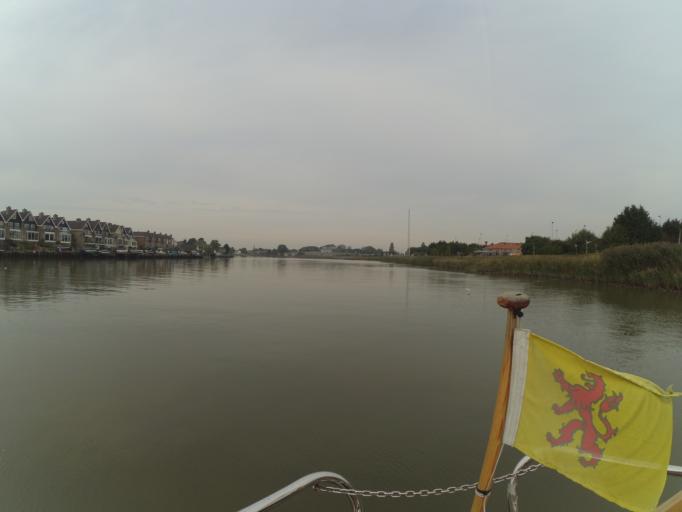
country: NL
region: South Holland
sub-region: Gemeente Krimpen aan den IJssel
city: Krimpen aan den IJssel
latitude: 51.9263
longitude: 4.6061
